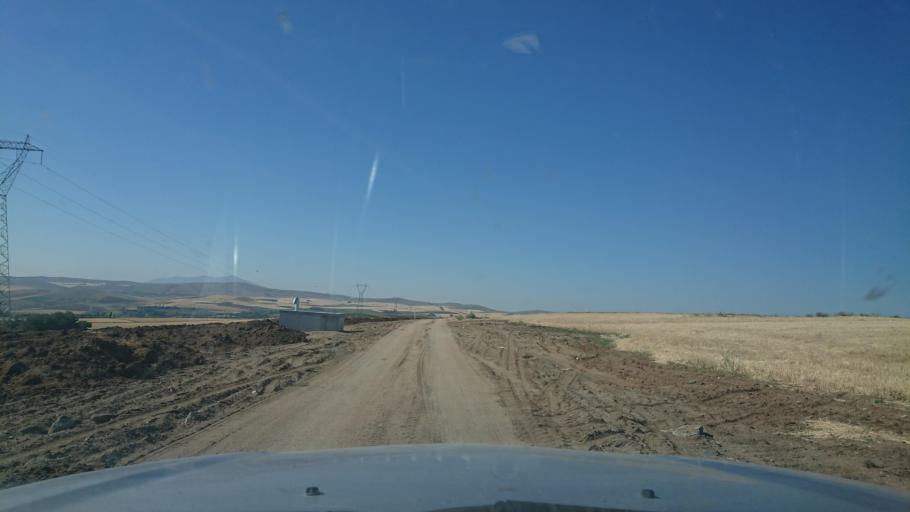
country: TR
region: Aksaray
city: Agacoren
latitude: 38.8416
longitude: 33.9442
